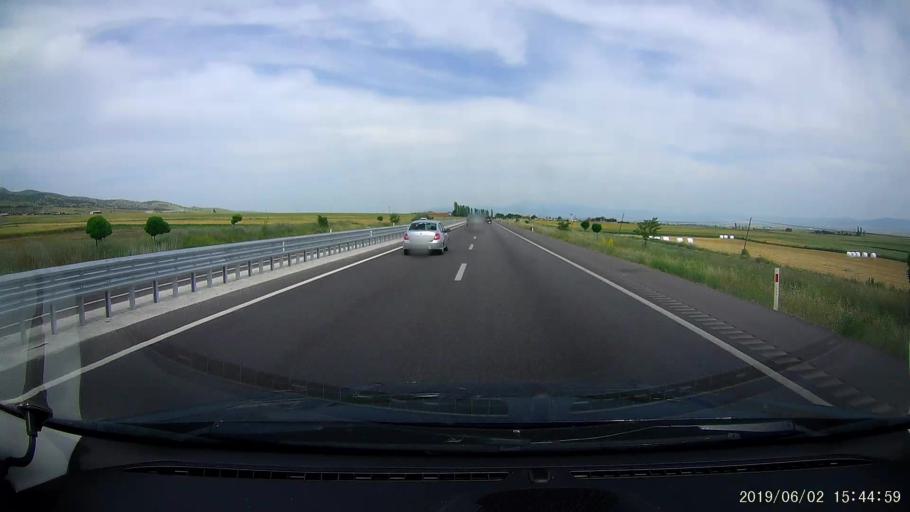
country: TR
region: Amasya
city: Alicik
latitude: 40.8655
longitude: 35.3732
